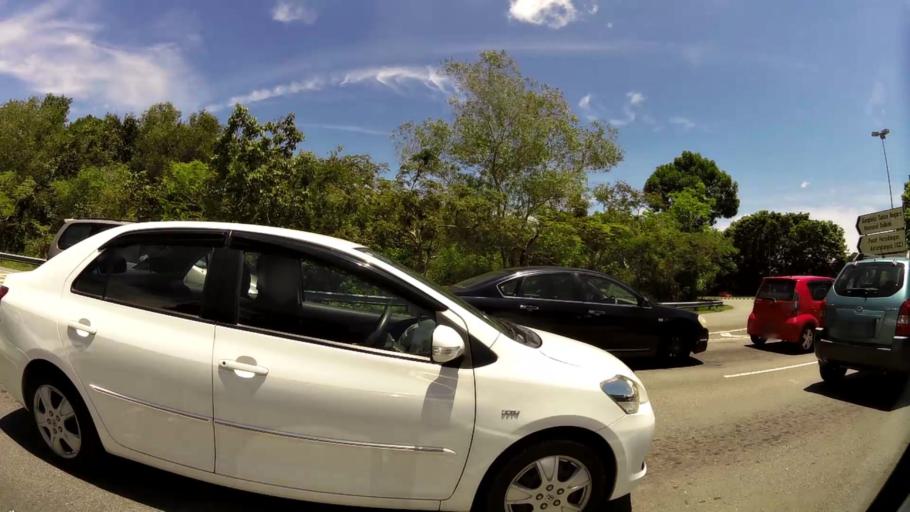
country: BN
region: Brunei and Muara
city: Bandar Seri Begawan
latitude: 4.9239
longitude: 114.9551
